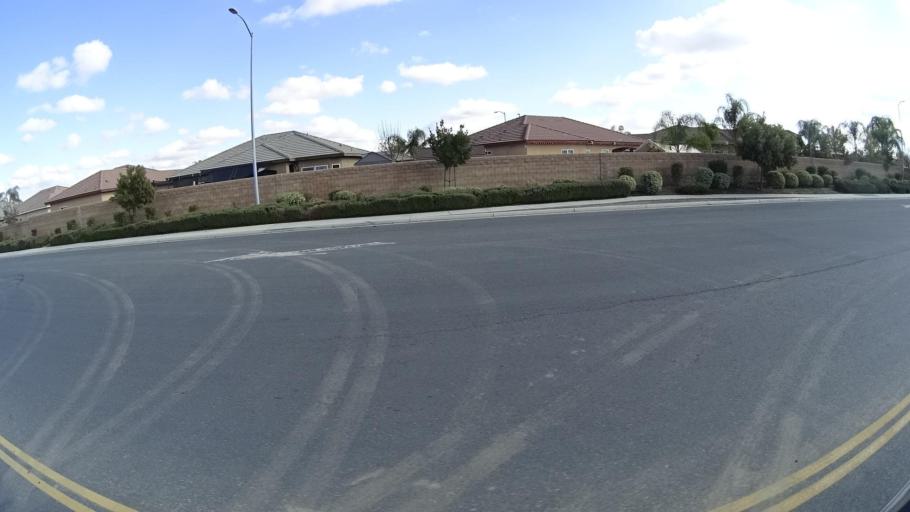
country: US
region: California
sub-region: Kern County
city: McFarland
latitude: 35.6824
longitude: -119.2407
